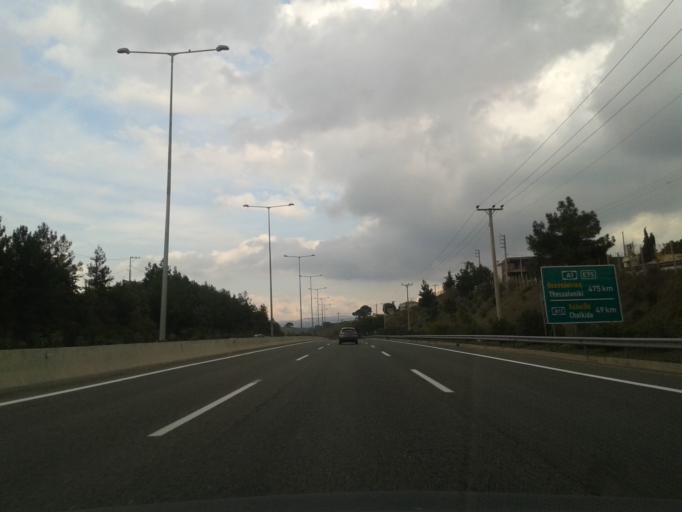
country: GR
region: Attica
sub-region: Nomarchia Anatolikis Attikis
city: Agios Stefanos
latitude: 38.1495
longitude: 23.8522
